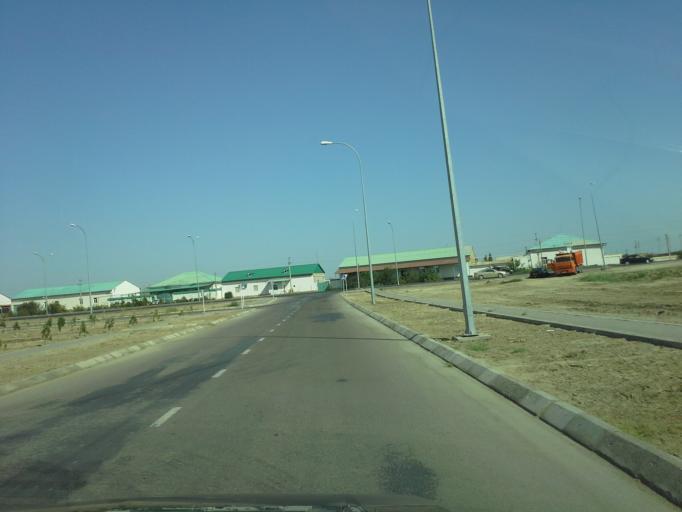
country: TM
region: Dasoguz
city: Dasoguz
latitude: 41.8125
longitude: 59.9576
